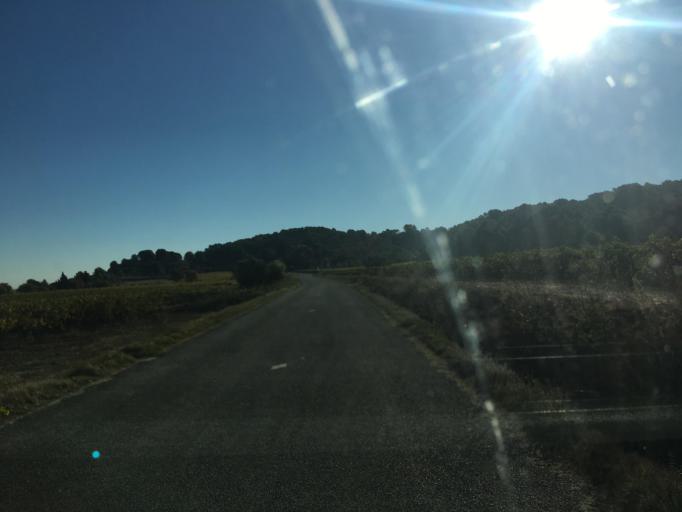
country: FR
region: Languedoc-Roussillon
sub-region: Departement de l'Aude
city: Fleury
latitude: 43.2350
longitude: 3.1561
